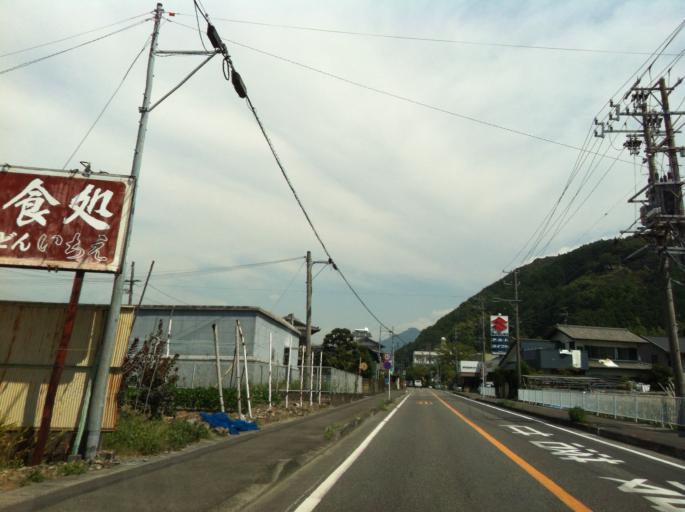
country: JP
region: Shizuoka
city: Shizuoka-shi
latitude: 35.0615
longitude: 138.3698
